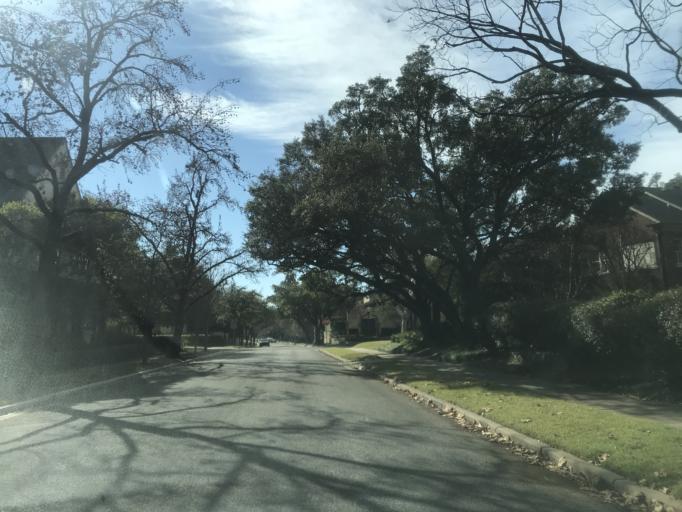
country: US
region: Texas
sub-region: Dallas County
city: Highland Park
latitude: 32.8268
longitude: -96.7945
